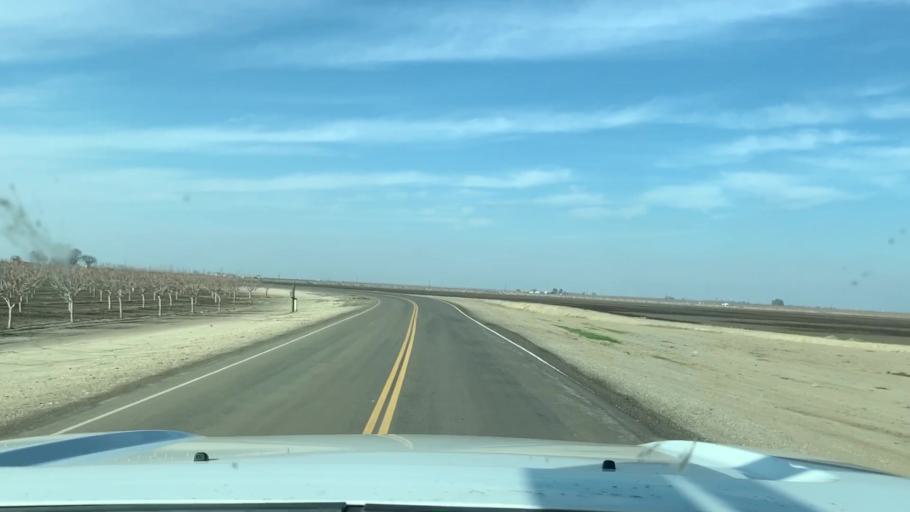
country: US
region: California
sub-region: Kern County
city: Buttonwillow
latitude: 35.4516
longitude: -119.5613
